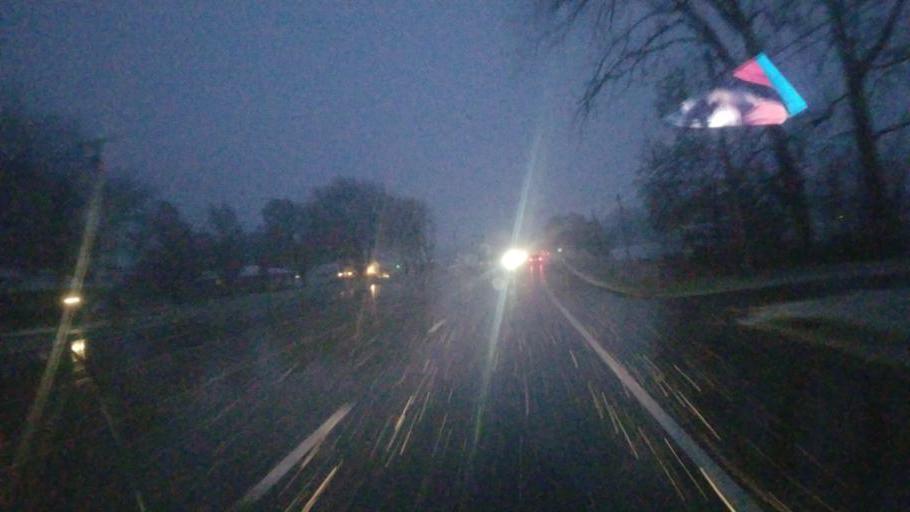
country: US
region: Ohio
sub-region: Richland County
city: Shelby
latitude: 40.8492
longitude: -82.6214
